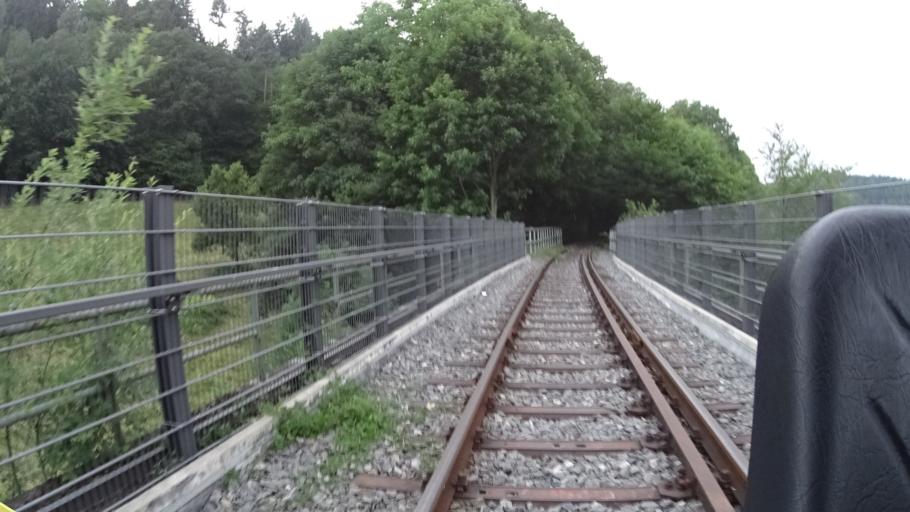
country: DE
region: Hesse
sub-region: Regierungsbezirk Darmstadt
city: Morlenbach
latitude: 49.5824
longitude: 8.7665
